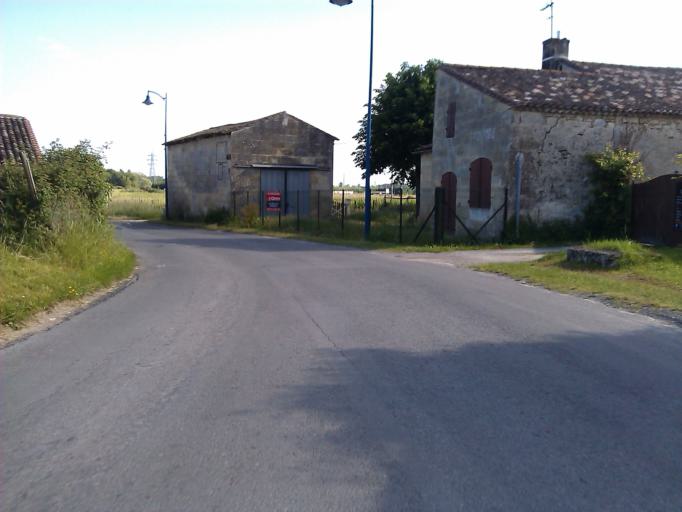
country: FR
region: Aquitaine
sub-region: Departement de la Gironde
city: Saint-Gervais
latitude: 45.0211
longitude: -0.4441
